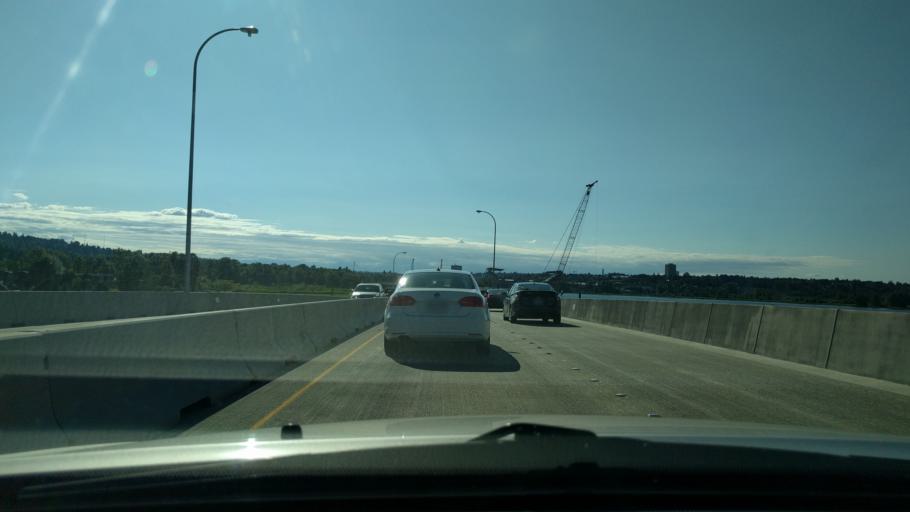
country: US
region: Washington
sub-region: King County
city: Medina
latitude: 47.6433
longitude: -122.2754
